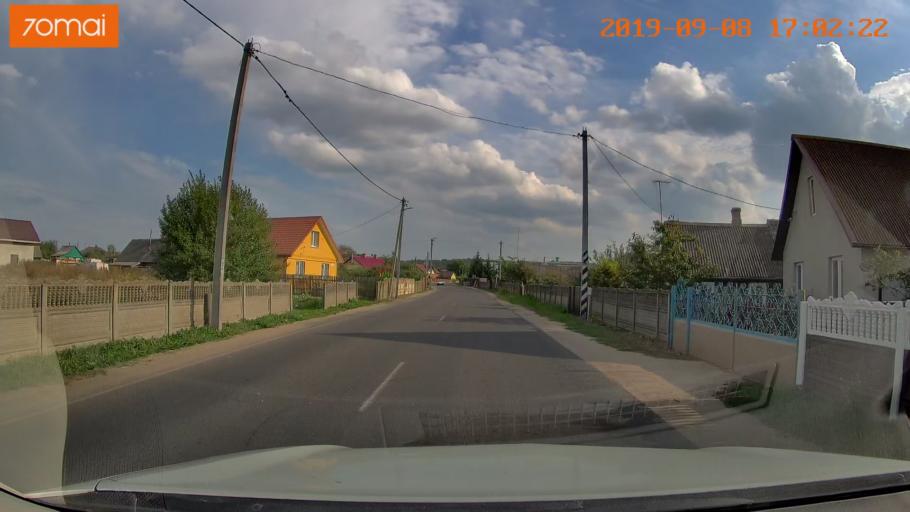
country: BY
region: Grodnenskaya
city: Hrodna
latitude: 53.7042
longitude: 23.9387
